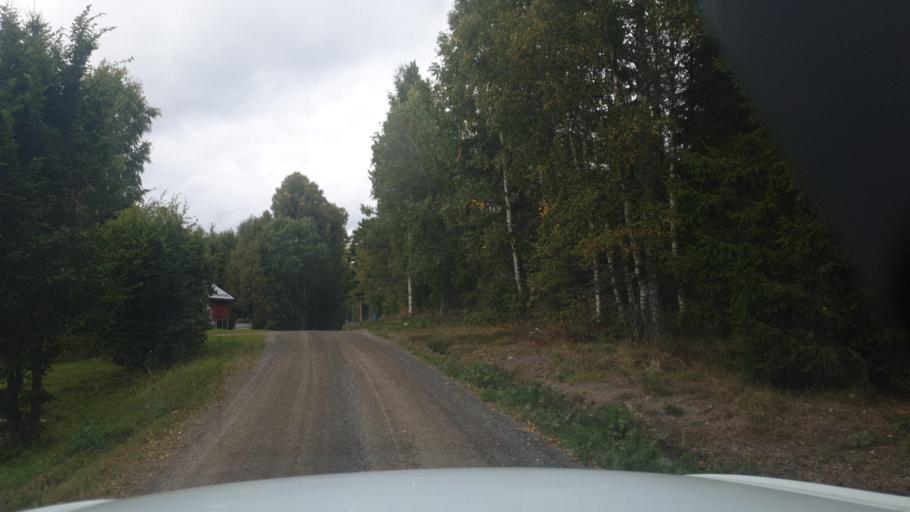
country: SE
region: Vaermland
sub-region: Torsby Kommun
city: Torsby
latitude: 59.9382
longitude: 12.8158
